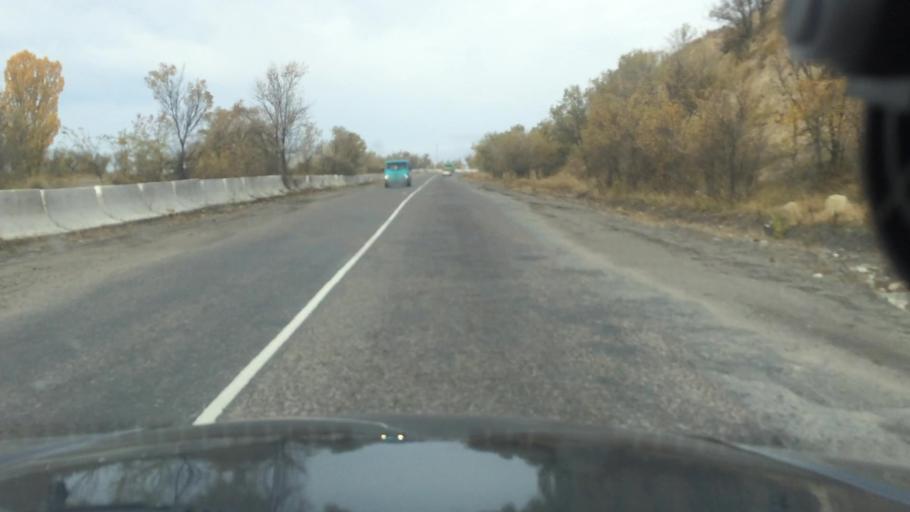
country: KG
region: Ysyk-Koel
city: Karakol
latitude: 42.5965
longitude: 78.3793
